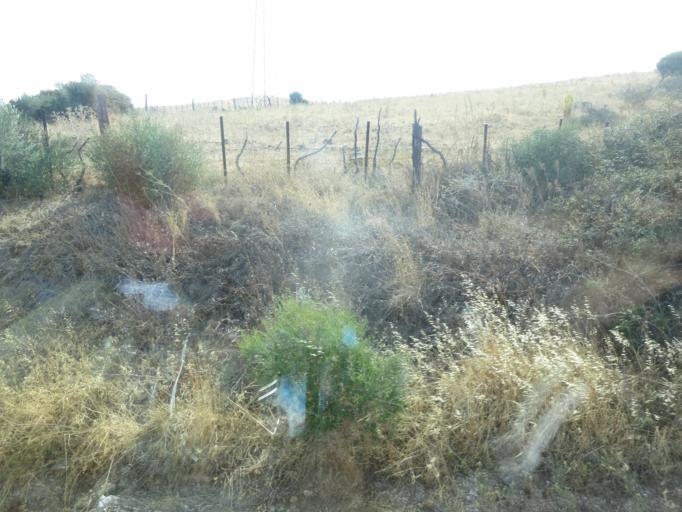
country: ES
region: Andalusia
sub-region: Provincia de Cadiz
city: Algeciras
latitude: 36.1023
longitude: -5.4638
